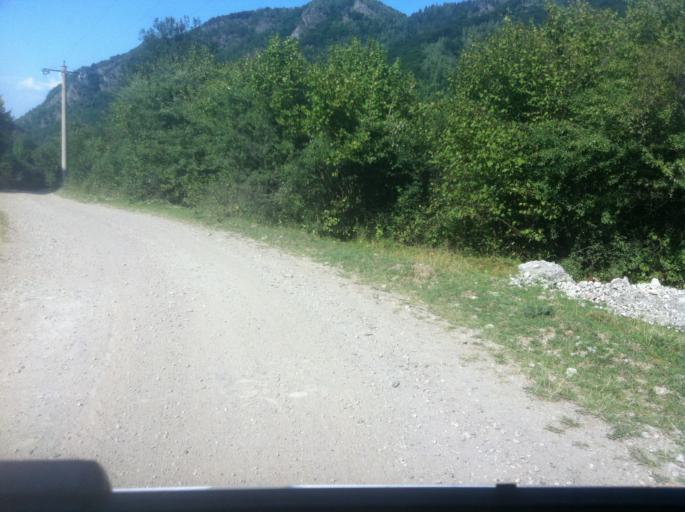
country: RO
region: Hunedoara
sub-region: Comuna Rau de Mori
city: Rau de Mori
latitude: 45.4531
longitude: 22.8962
